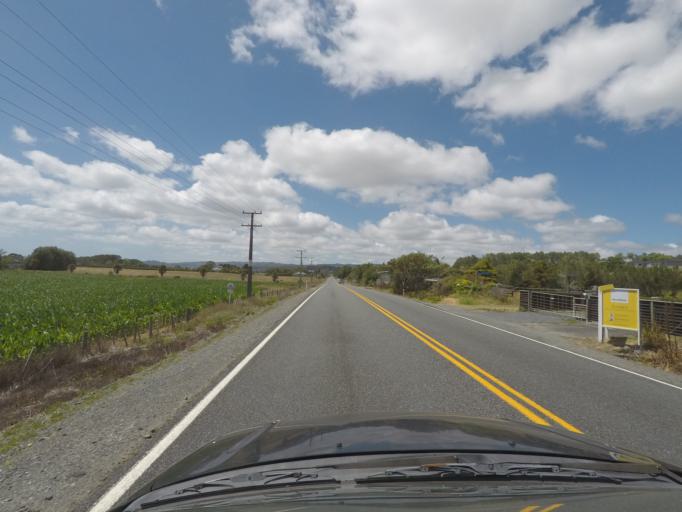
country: NZ
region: Northland
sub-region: Whangarei
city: Ruakaka
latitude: -36.0004
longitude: 174.4752
